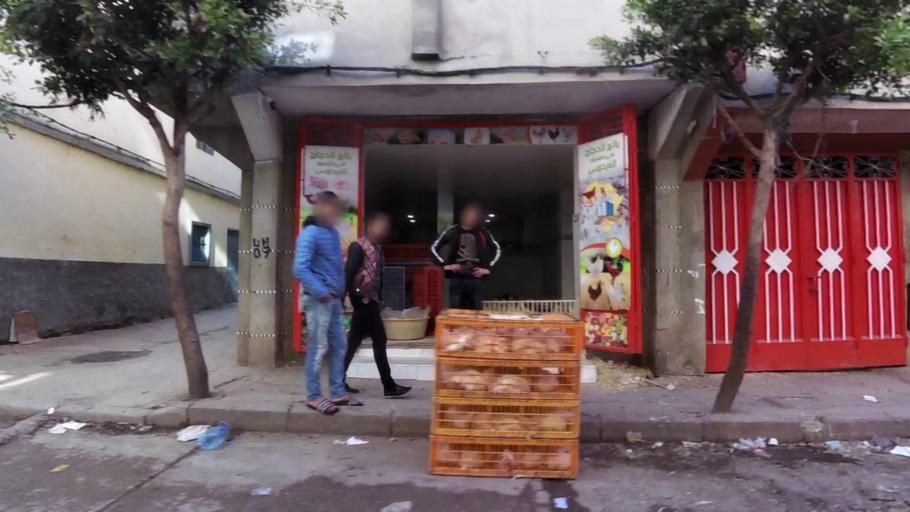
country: MA
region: Tanger-Tetouan
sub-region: Tanger-Assilah
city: Tangier
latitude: 35.7610
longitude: -5.7913
